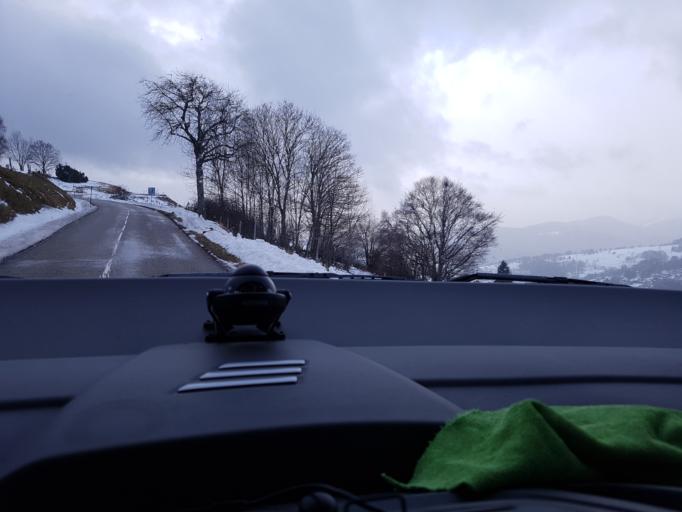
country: FR
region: Alsace
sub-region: Departement du Haut-Rhin
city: Soultzeren
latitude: 48.0823
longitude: 7.1125
